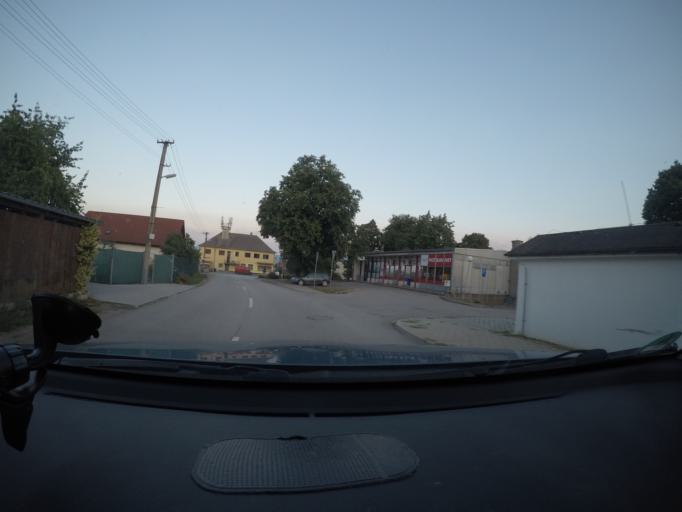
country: SK
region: Trenciansky
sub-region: Okres Trencin
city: Trencin
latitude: 48.8670
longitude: 17.9441
